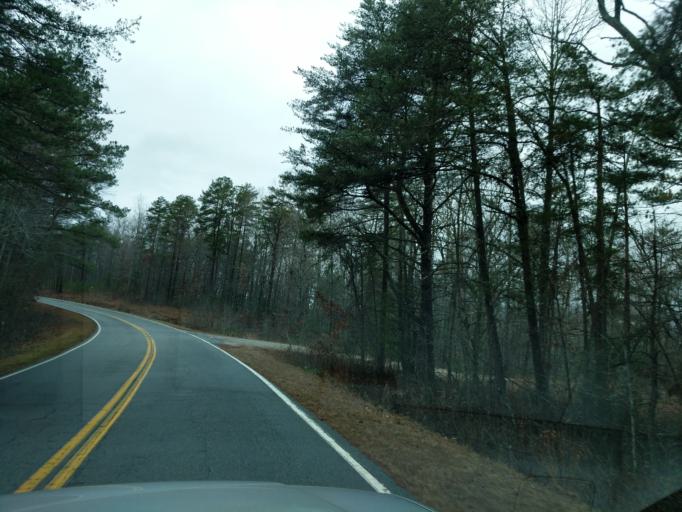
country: US
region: South Carolina
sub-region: Oconee County
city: Walhalla
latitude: 34.7949
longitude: -83.1785
